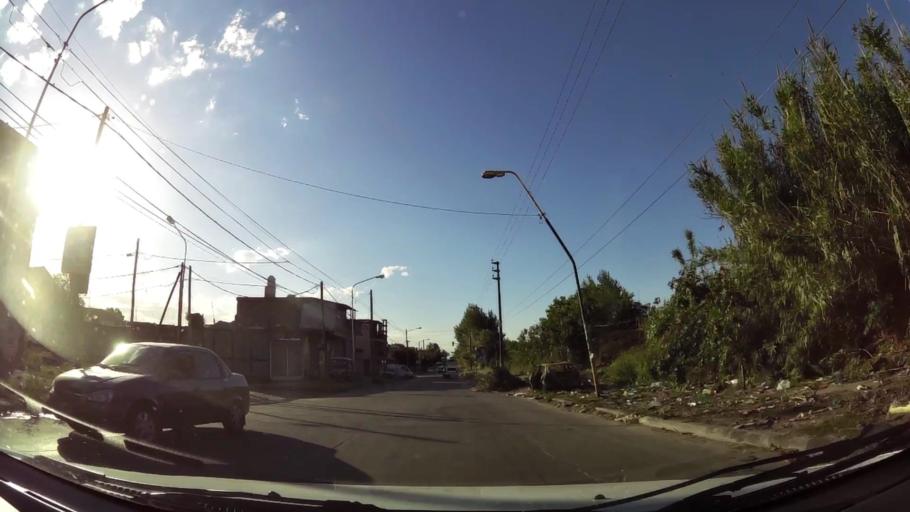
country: AR
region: Buenos Aires
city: Caseros
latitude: -34.5724
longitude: -58.5861
